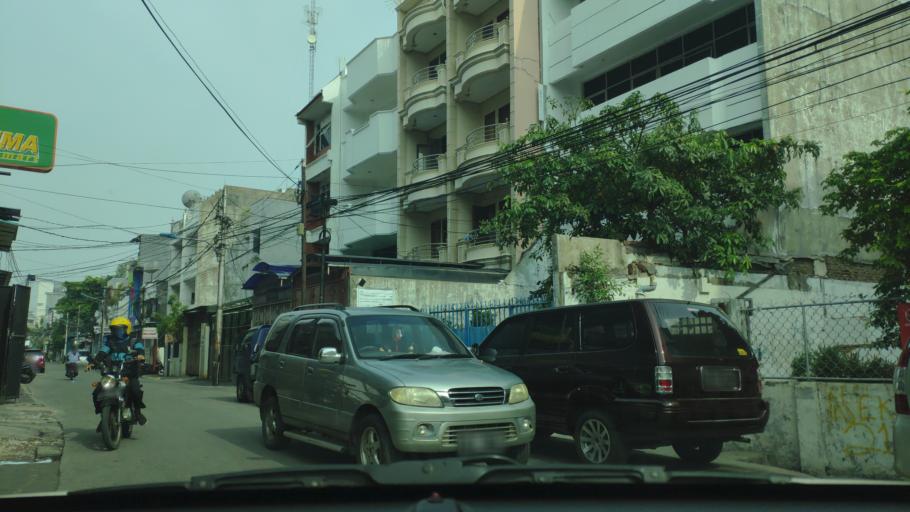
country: ID
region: Jakarta Raya
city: Jakarta
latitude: -6.1588
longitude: 106.8151
